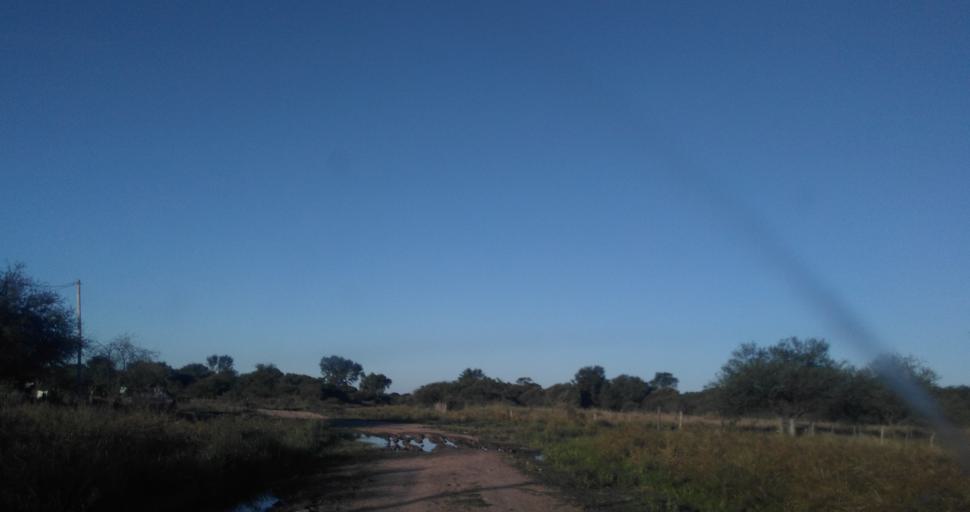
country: AR
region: Chaco
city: Fontana
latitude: -27.3867
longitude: -58.9738
